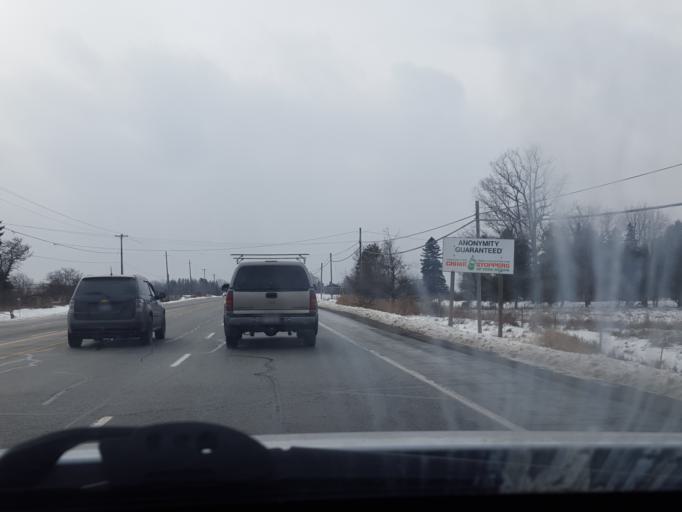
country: CA
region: Ontario
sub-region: York
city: Richmond Hill
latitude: 43.9385
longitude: -79.4841
